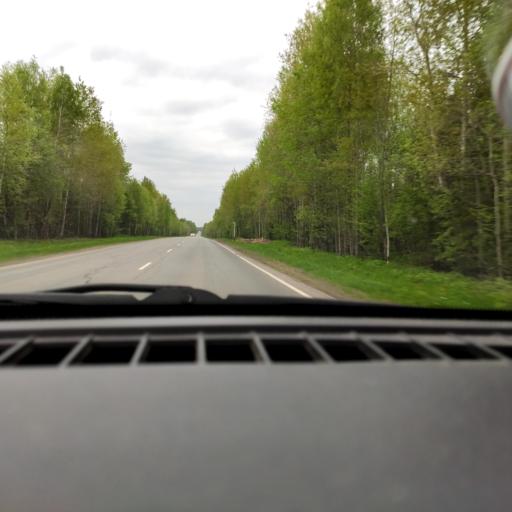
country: RU
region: Perm
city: Polazna
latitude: 58.2707
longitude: 56.1671
